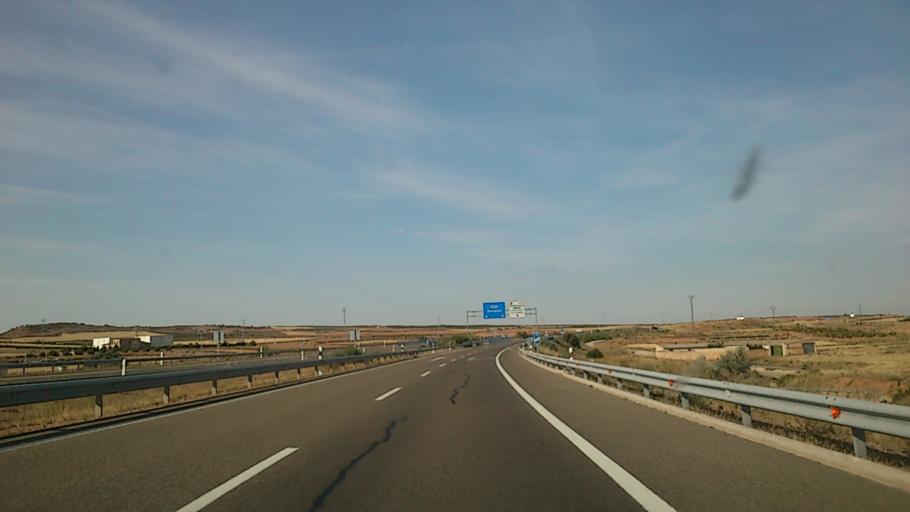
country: ES
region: Aragon
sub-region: Provincia de Zaragoza
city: Longares
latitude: 41.4026
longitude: -1.1787
